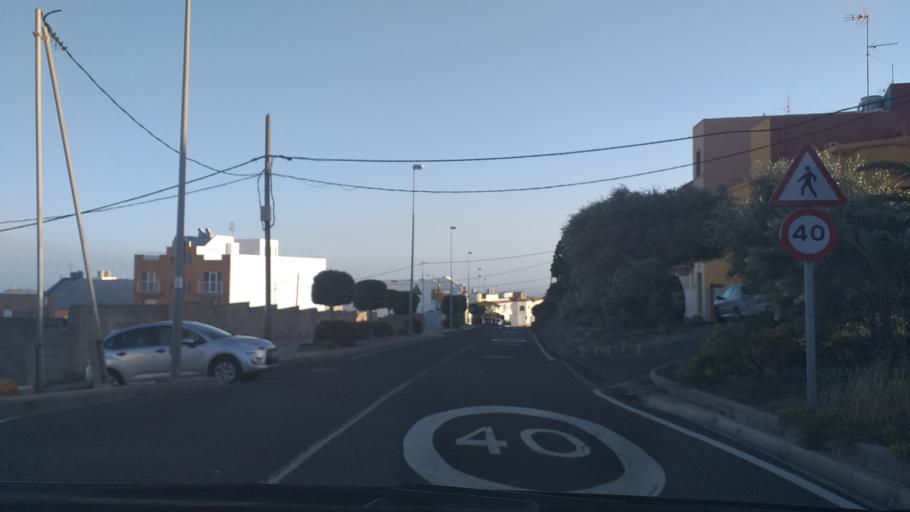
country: ES
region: Canary Islands
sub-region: Provincia de Las Palmas
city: Ingenio
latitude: 27.9220
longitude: -15.4488
